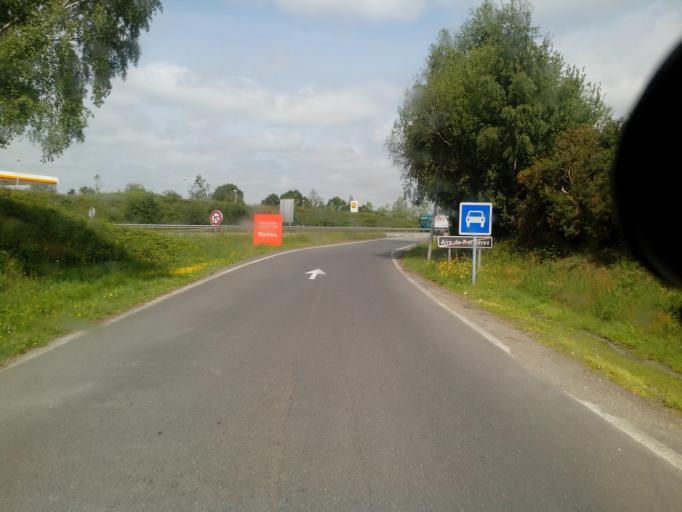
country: FR
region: Pays de la Loire
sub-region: Departement de la Loire-Atlantique
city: Treillieres
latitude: 47.3373
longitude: -1.6533
